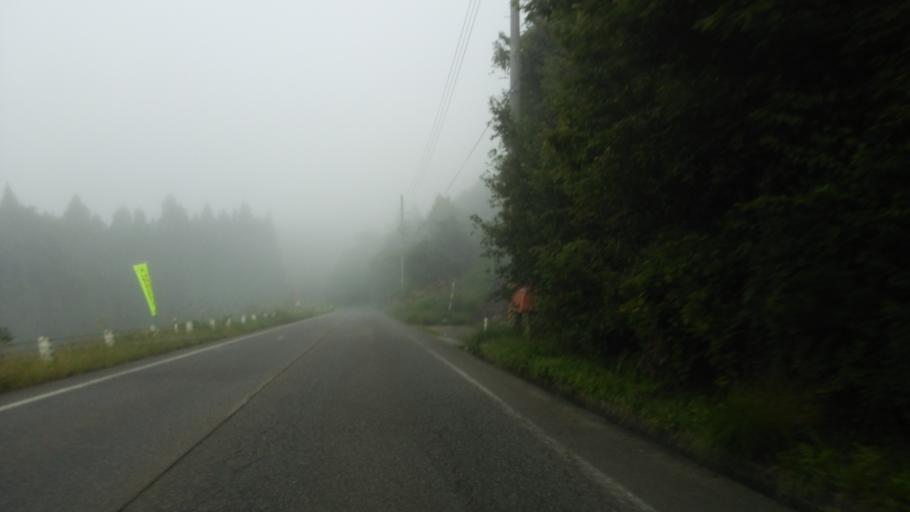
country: JP
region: Fukushima
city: Kitakata
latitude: 37.5796
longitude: 139.7786
